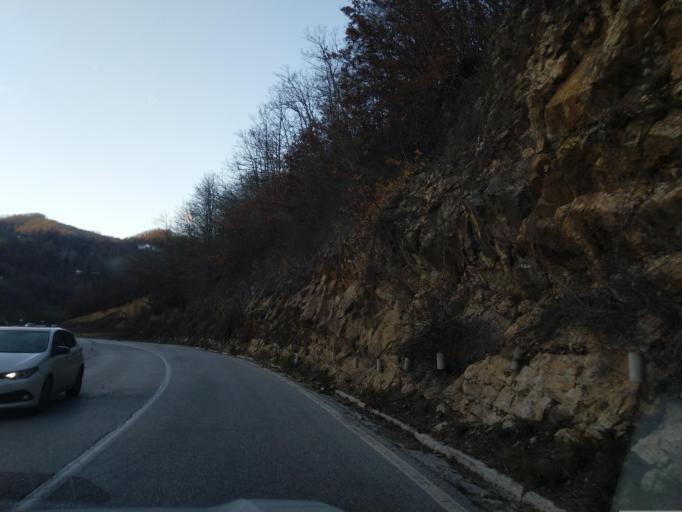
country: RS
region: Central Serbia
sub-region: Zlatiborski Okrug
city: Kosjeric
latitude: 43.9679
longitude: 19.9579
